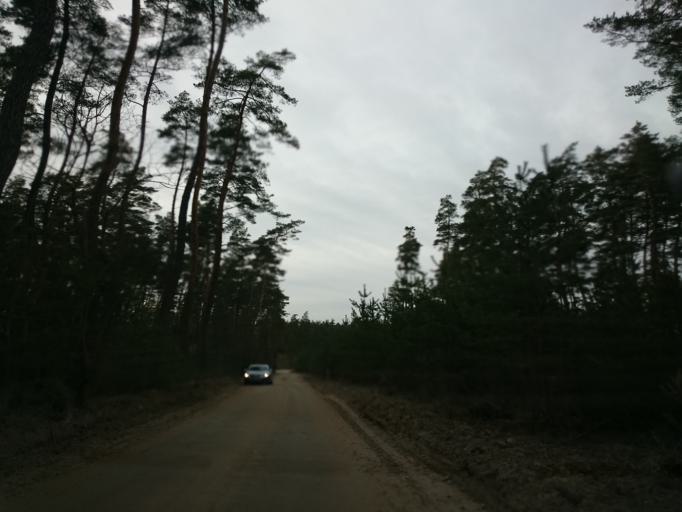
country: LV
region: Garkalne
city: Garkalne
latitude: 57.0276
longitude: 24.3846
